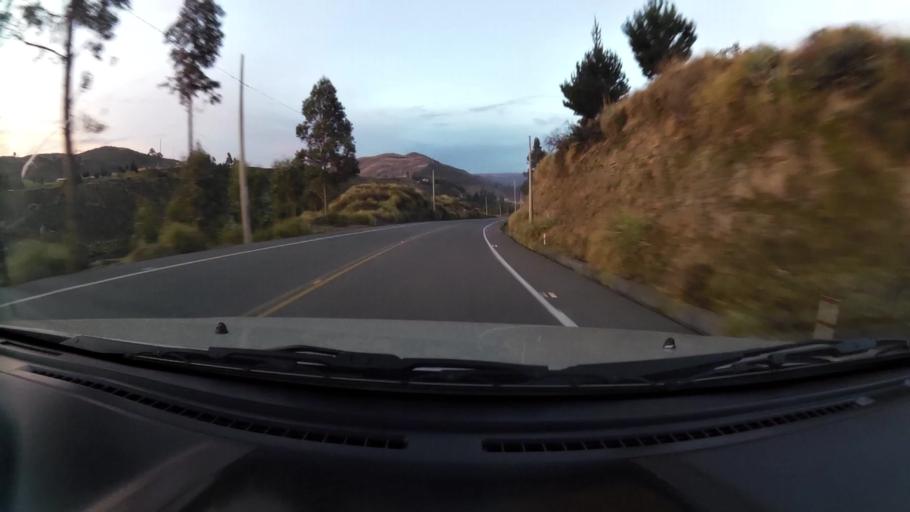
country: EC
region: Chimborazo
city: Riobamba
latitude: -1.9453
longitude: -78.7105
